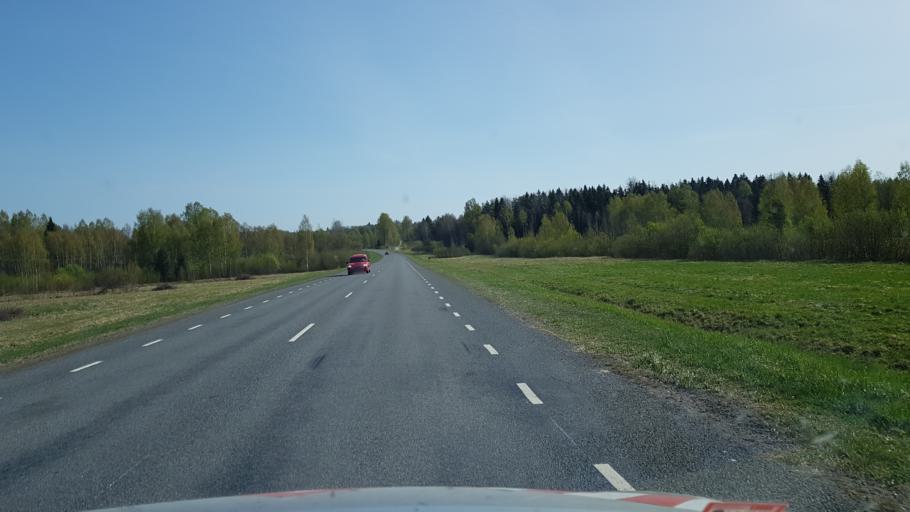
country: EE
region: Viljandimaa
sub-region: Karksi vald
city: Karksi-Nuia
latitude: 58.1902
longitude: 25.5229
